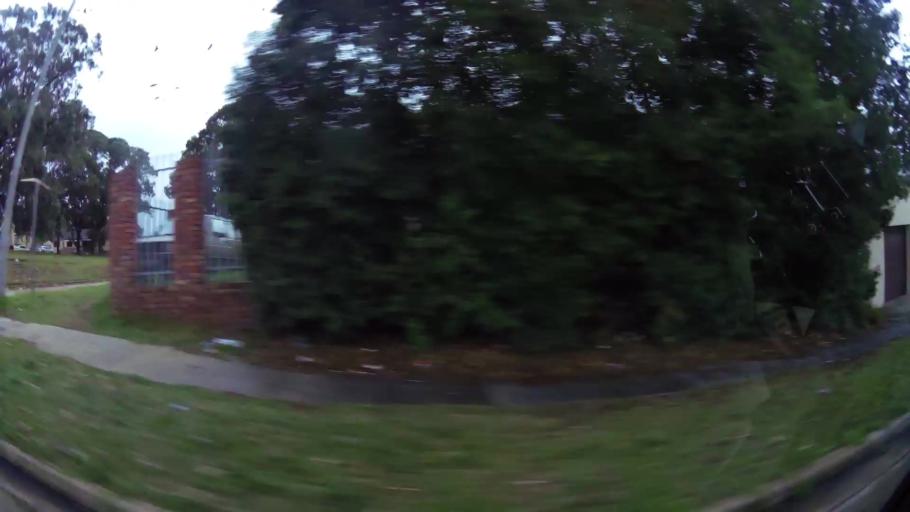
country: ZA
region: Eastern Cape
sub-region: Nelson Mandela Bay Metropolitan Municipality
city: Port Elizabeth
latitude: -33.9433
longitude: 25.5945
